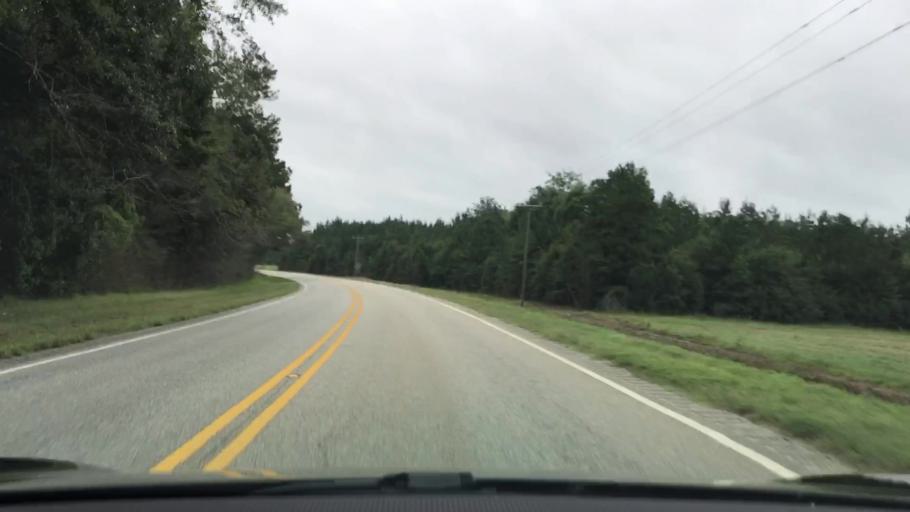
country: US
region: Alabama
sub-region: Coffee County
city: Elba
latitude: 31.3713
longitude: -86.0951
